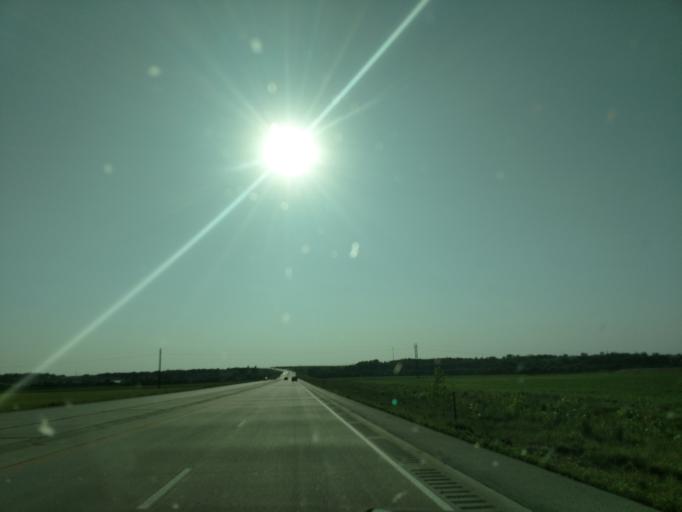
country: US
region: Nebraska
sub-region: Sarpy County
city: Offutt Air Force Base
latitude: 41.0797
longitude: -95.9050
